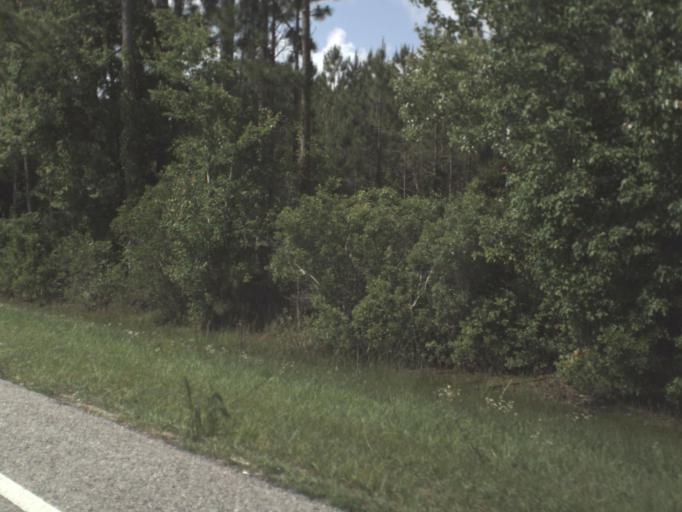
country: US
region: Florida
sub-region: Saint Johns County
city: Butler Beach
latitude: 29.7037
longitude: -81.2990
